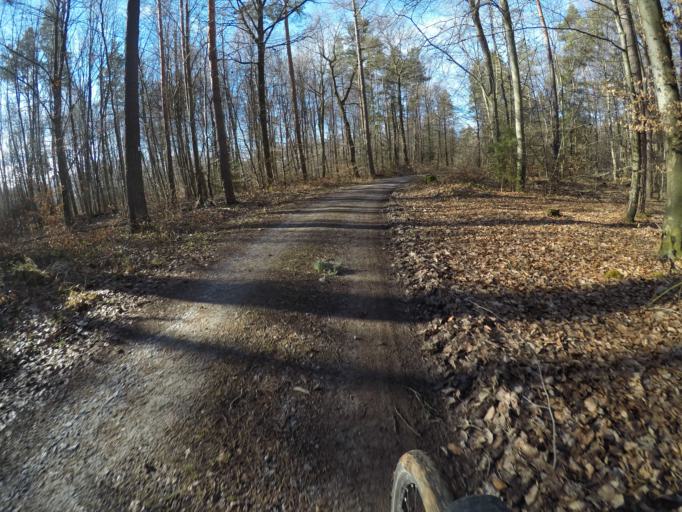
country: DE
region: Baden-Wuerttemberg
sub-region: Regierungsbezirk Stuttgart
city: Steinenbronn
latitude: 48.6915
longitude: 9.1014
